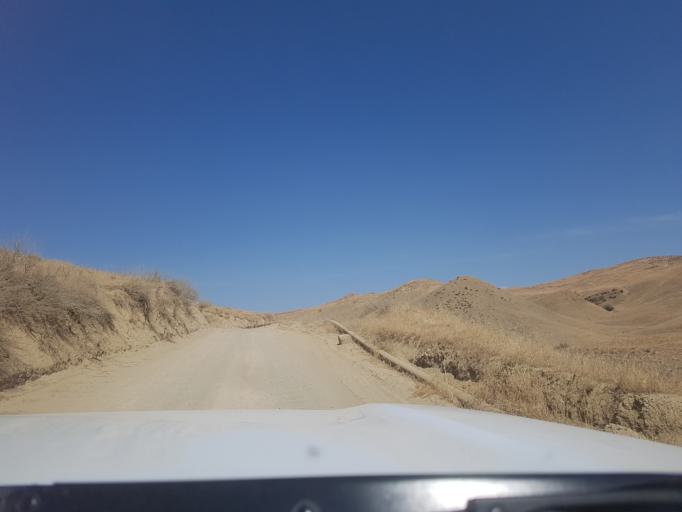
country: TM
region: Ahal
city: Baharly
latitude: 38.2603
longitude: 56.8885
